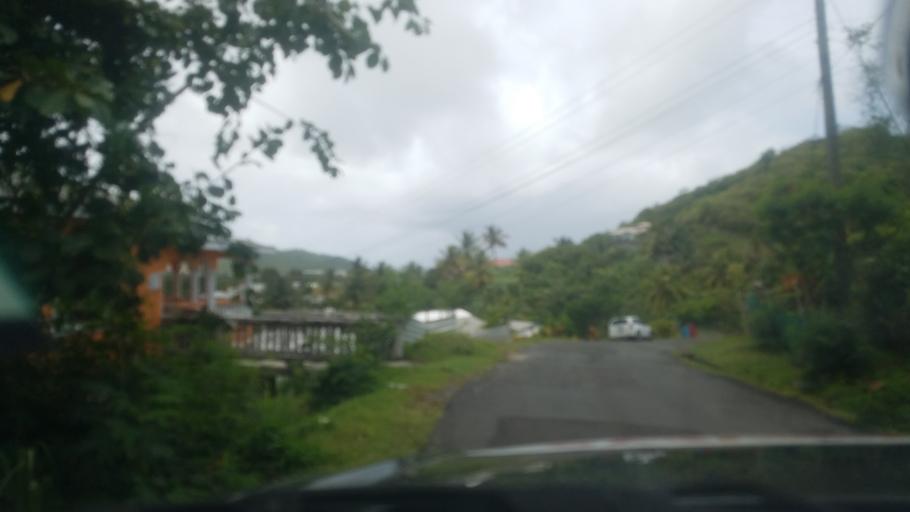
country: LC
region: Laborie Quarter
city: Laborie
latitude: 13.7436
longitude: -60.9631
